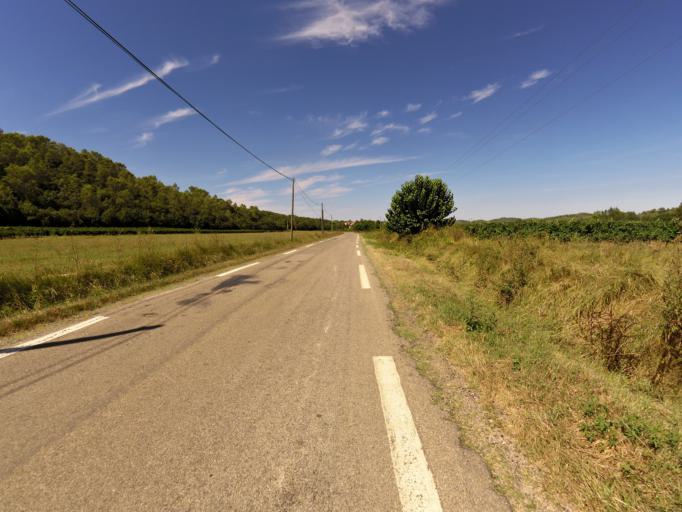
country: FR
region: Languedoc-Roussillon
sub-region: Departement du Gard
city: Quissac
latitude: 43.8651
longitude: 4.0400
